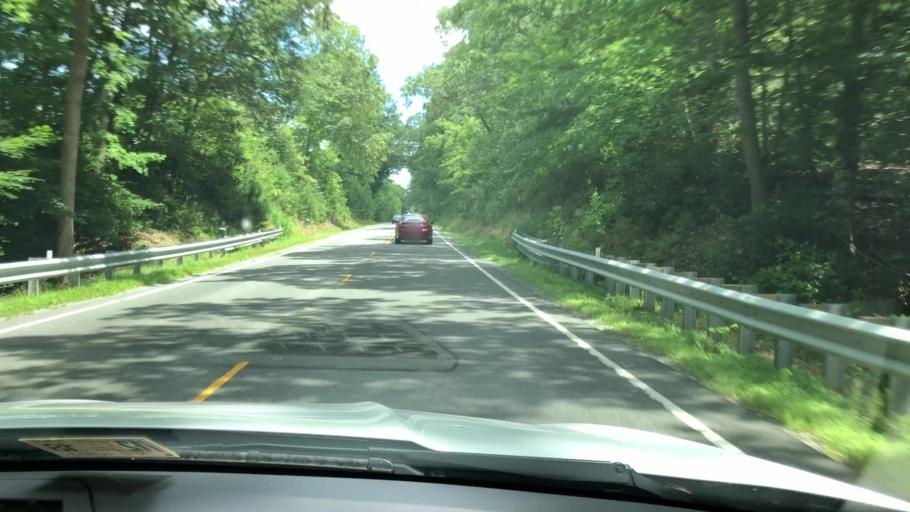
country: US
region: Virginia
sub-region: Lancaster County
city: Lancaster
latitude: 37.7692
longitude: -76.4899
